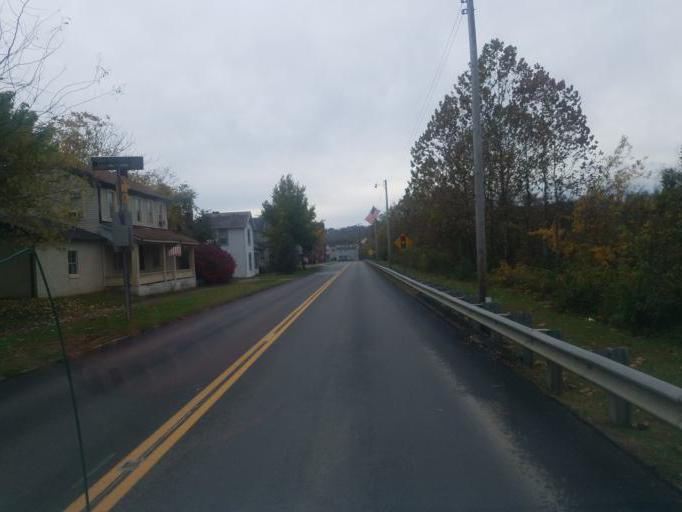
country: US
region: Ohio
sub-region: Washington County
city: Devola
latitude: 39.5301
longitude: -81.5086
